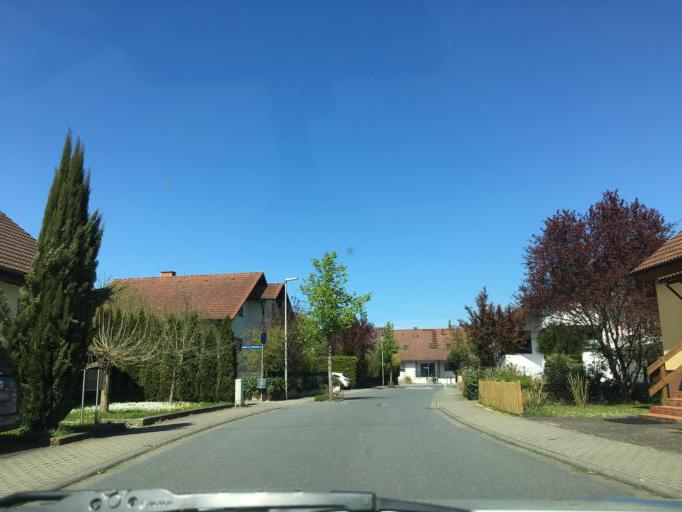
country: DE
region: Hesse
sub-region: Regierungsbezirk Darmstadt
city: Gross-Zimmern
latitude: 49.8676
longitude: 8.8352
